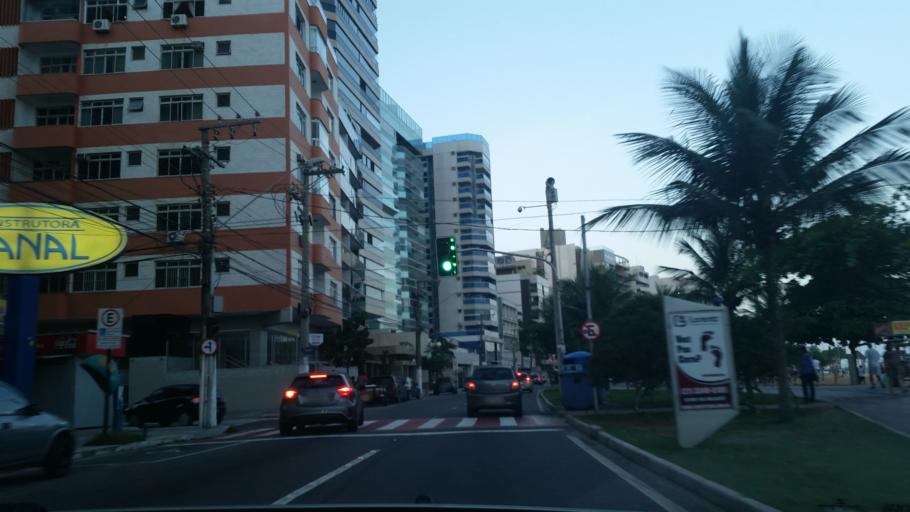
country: BR
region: Espirito Santo
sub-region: Vila Velha
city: Vila Velha
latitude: -20.3329
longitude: -40.2785
